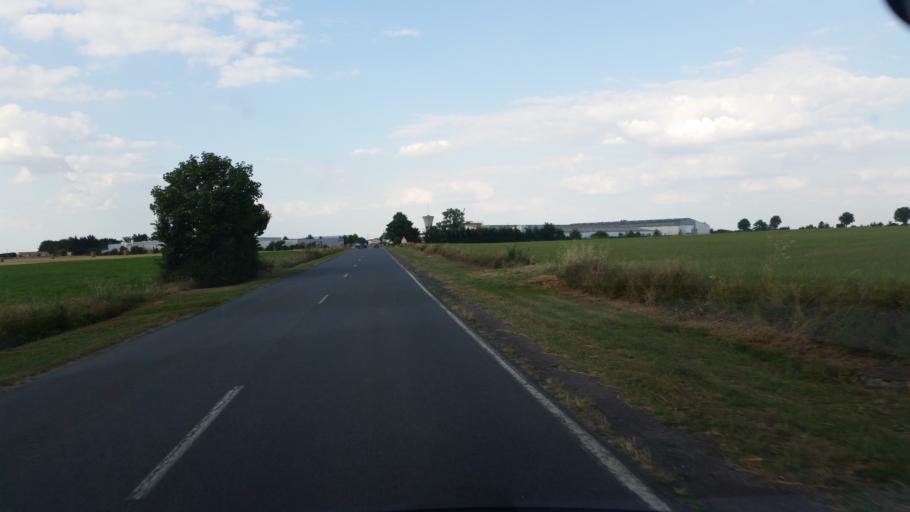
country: FR
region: Poitou-Charentes
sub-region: Departement de la Charente-Maritime
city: Andilly
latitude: 46.2576
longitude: -1.0179
